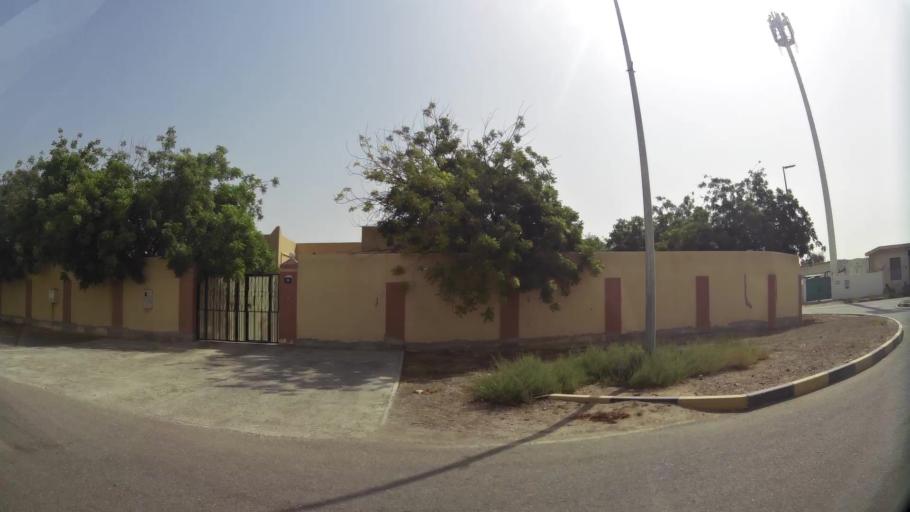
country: AE
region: Ash Shariqah
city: Sharjah
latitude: 25.3486
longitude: 55.4207
